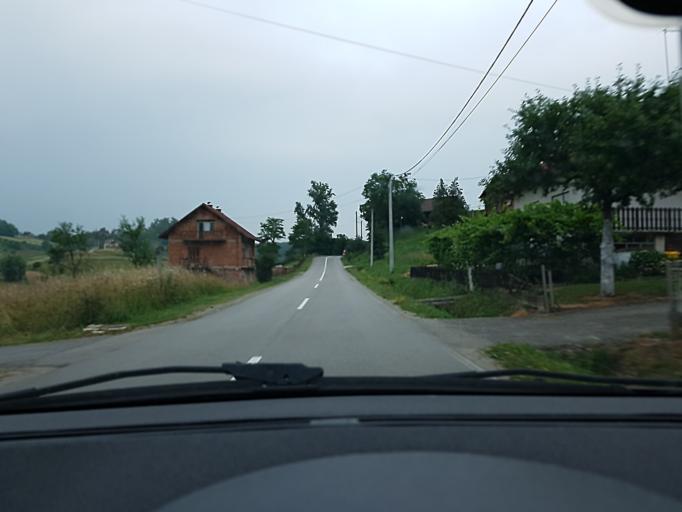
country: HR
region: Zagrebacka
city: Jakovlje
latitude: 45.9721
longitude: 15.8323
